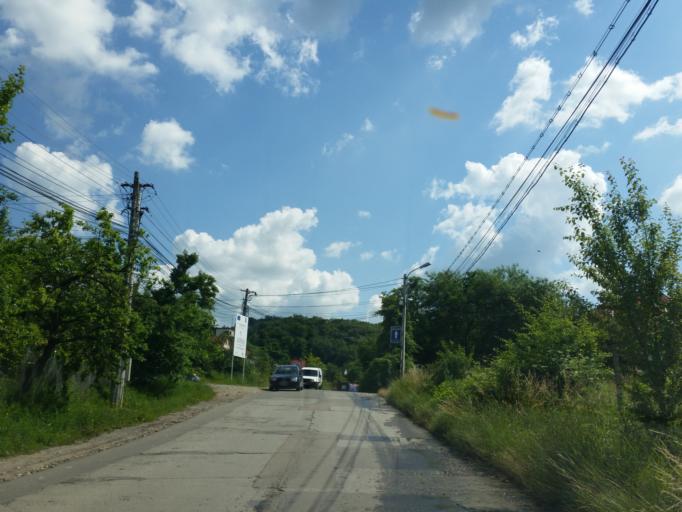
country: RO
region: Cluj
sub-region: Comuna Feleacu
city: Feleacu
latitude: 46.7290
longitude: 23.5866
